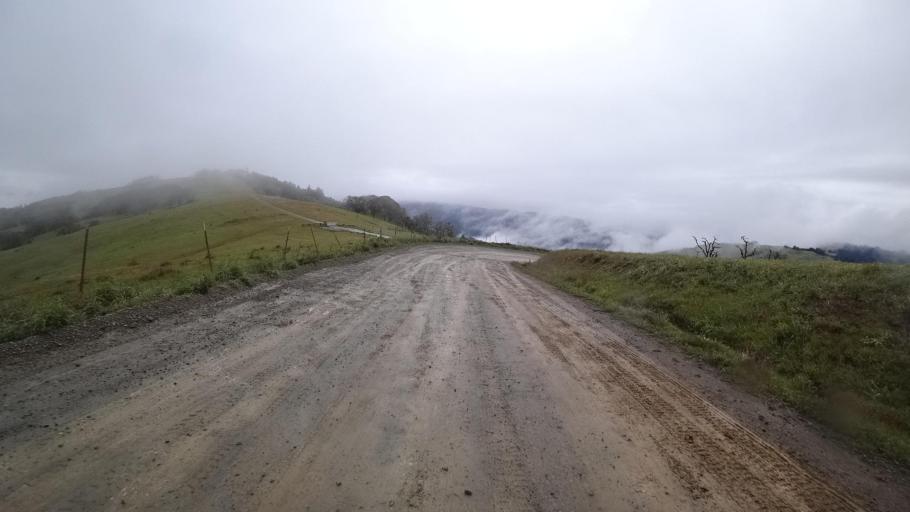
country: US
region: California
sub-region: Humboldt County
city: Westhaven-Moonstone
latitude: 41.1479
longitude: -123.8926
